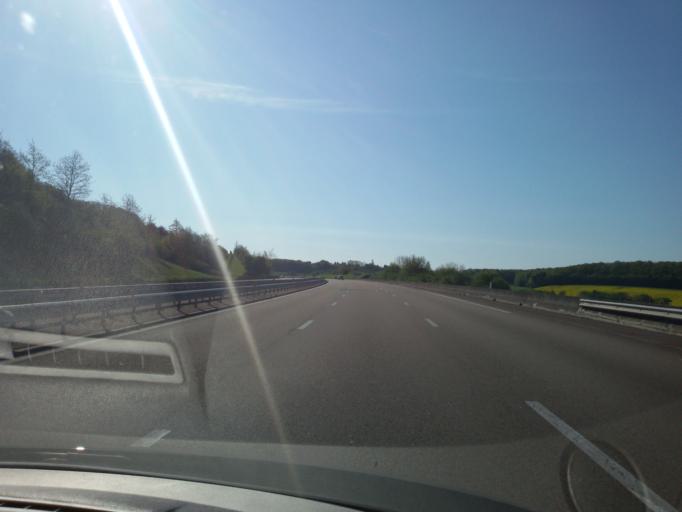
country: FR
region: Bourgogne
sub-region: Departement de l'Yonne
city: Cezy
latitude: 47.9315
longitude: 3.2520
